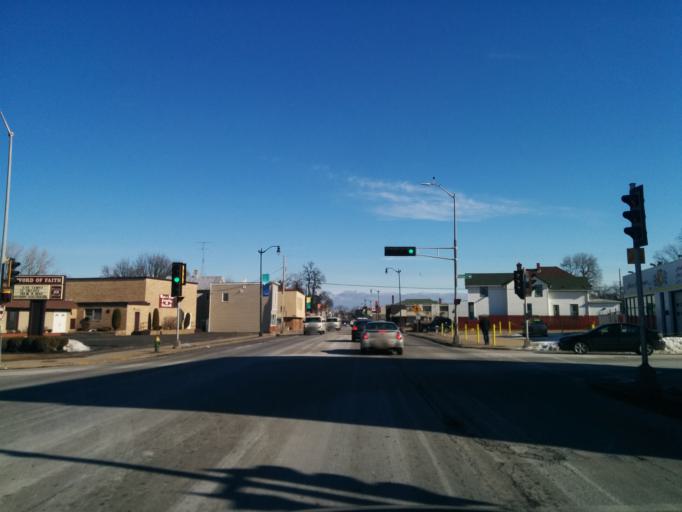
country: US
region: Wisconsin
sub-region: Racine County
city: Racine
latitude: 42.7144
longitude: -87.8024
